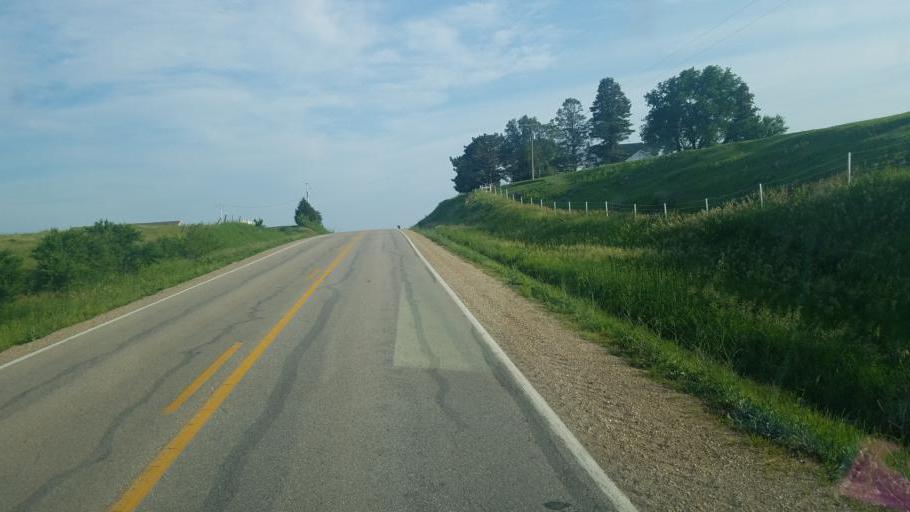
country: US
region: Iowa
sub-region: Tama County
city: Tama
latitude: 41.9736
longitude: -92.7085
